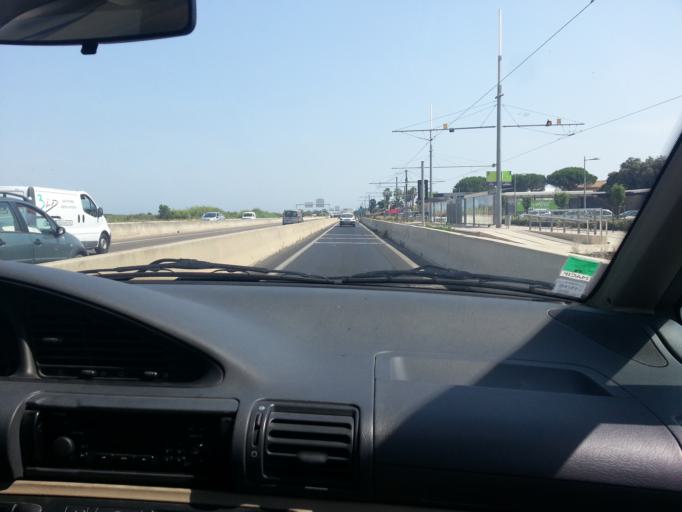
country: FR
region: Languedoc-Roussillon
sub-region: Departement de l'Herault
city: Perols
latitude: 43.5659
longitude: 3.9571
